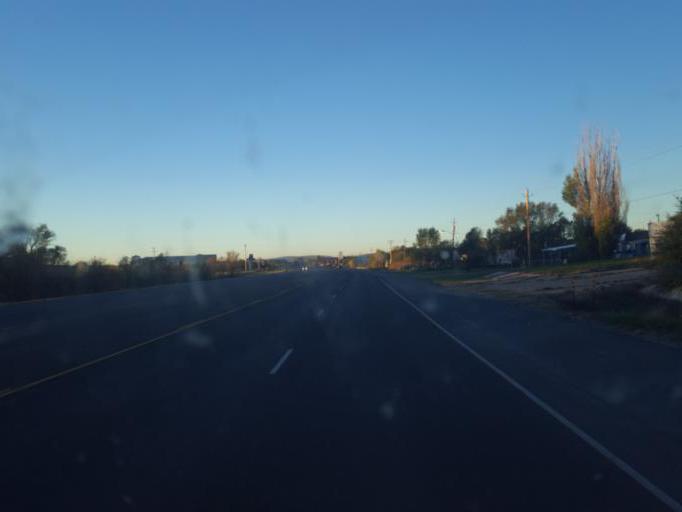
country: US
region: New Mexico
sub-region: San Miguel County
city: Las Vegas
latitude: 35.6197
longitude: -105.2072
